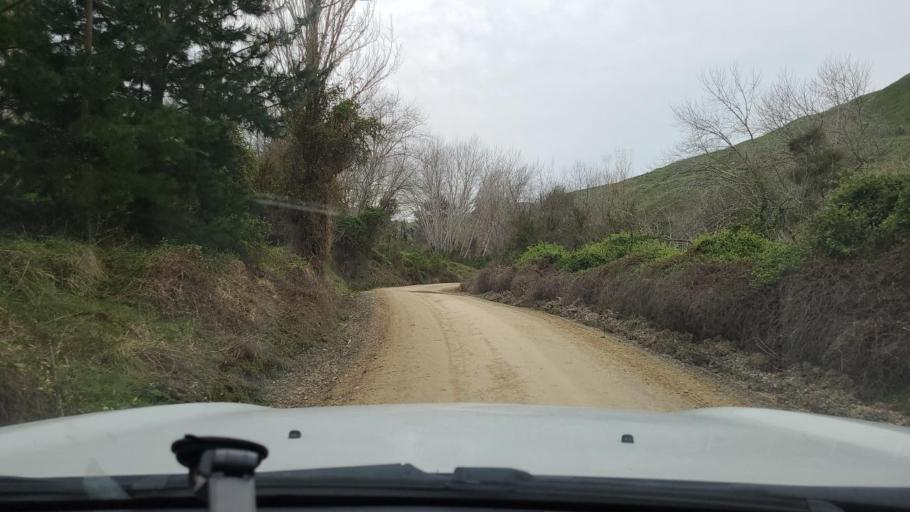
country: NZ
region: Gisborne
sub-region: Gisborne District
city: Gisborne
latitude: -38.5054
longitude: 178.0632
